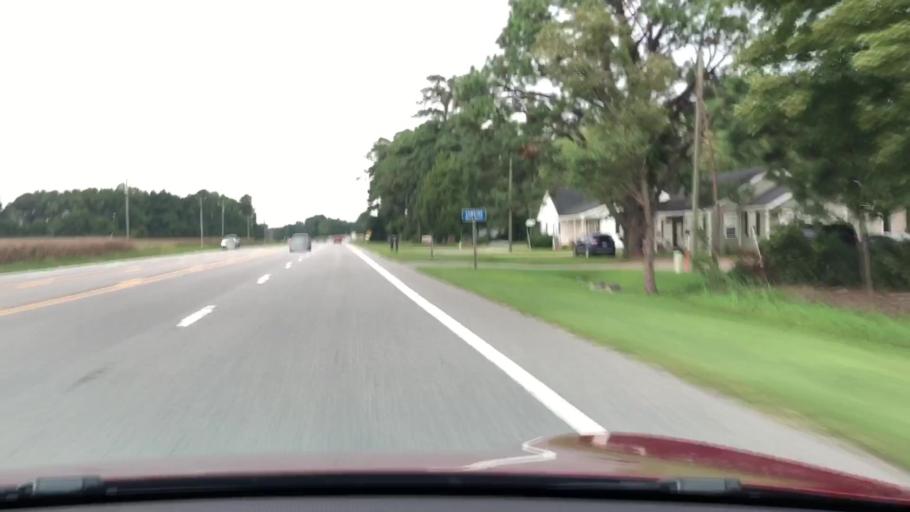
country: US
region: North Carolina
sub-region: Currituck County
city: Currituck
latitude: 36.4312
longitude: -76.0074
